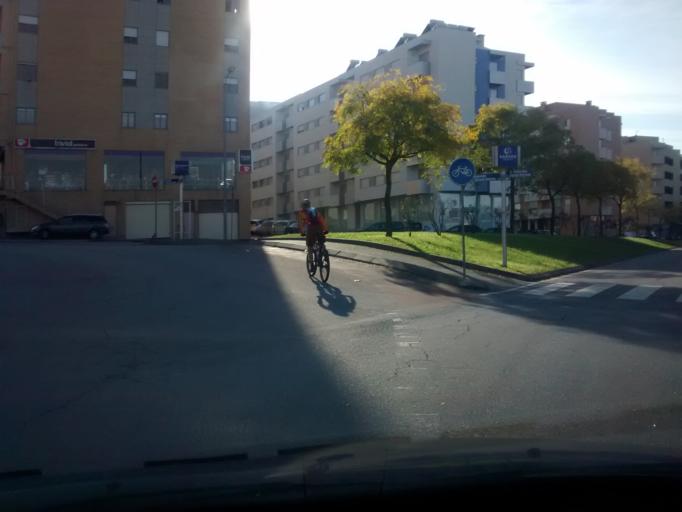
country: PT
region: Braga
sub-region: Braga
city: Braga
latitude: 41.5403
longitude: -8.3988
